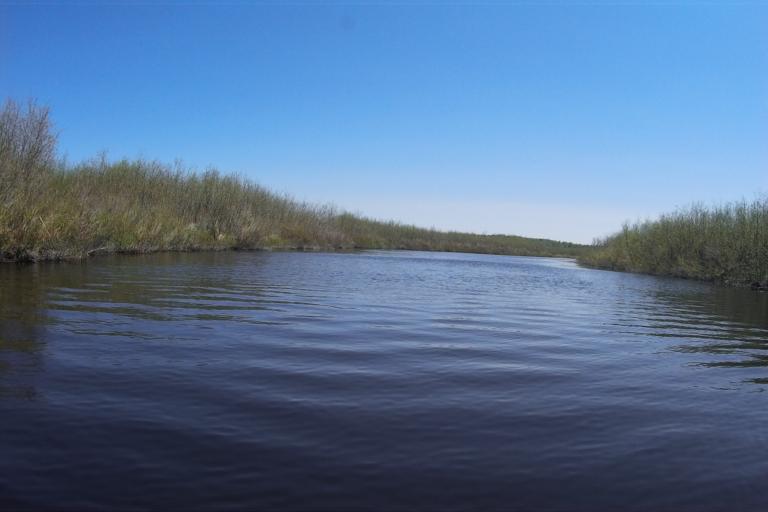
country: CA
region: Ontario
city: Powassan
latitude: 46.1602
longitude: -79.2571
